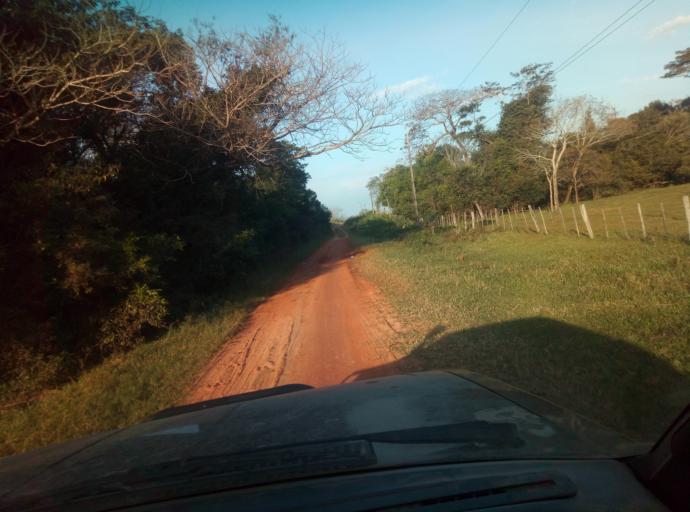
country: PY
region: Caaguazu
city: Doctor Cecilio Baez
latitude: -25.1519
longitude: -56.2485
